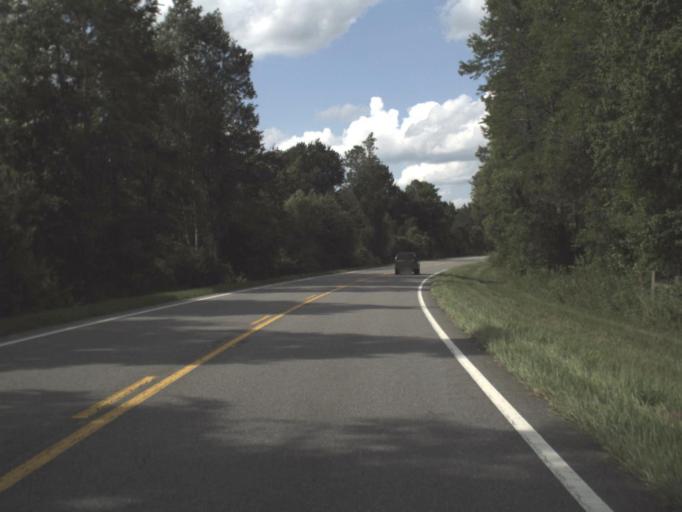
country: US
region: Florida
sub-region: Madison County
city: Madison
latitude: 30.3894
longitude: -83.6573
